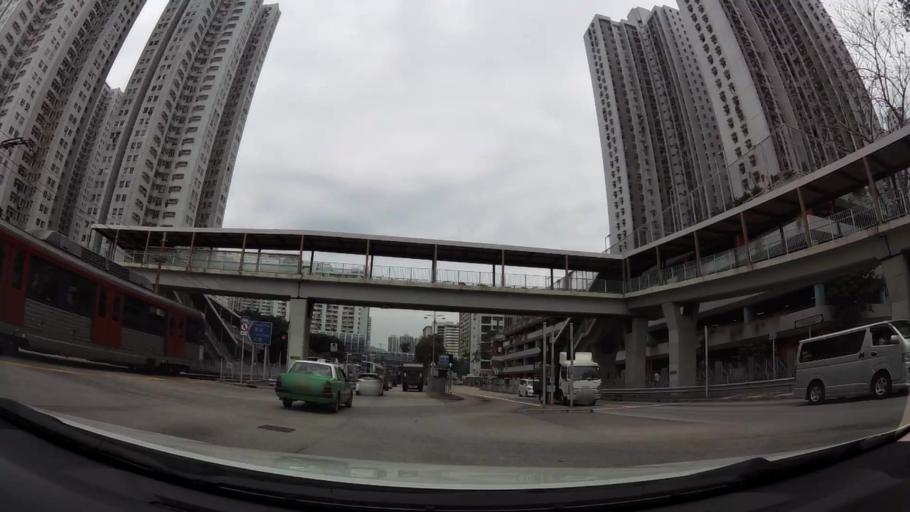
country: HK
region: Tuen Mun
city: Tuen Mun
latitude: 22.3837
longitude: 113.9751
